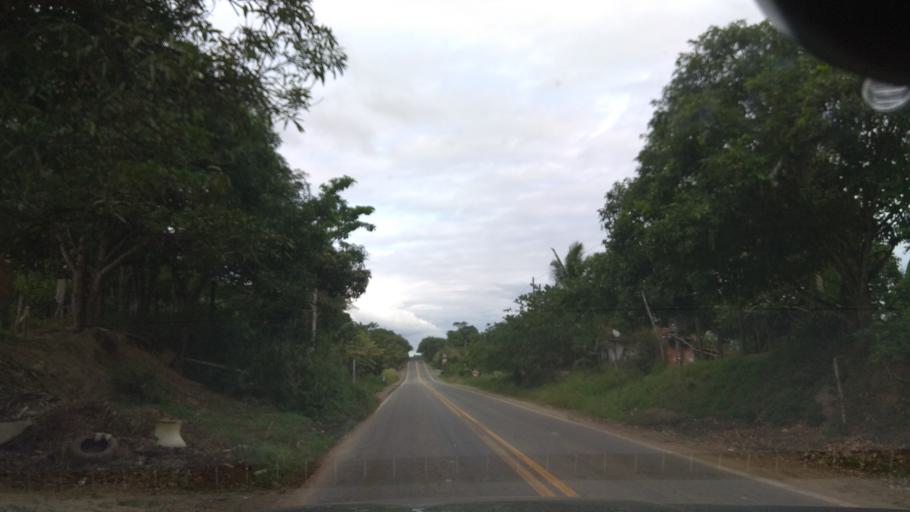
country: BR
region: Bahia
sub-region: Ipiau
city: Ipiau
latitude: -14.1657
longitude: -39.6879
